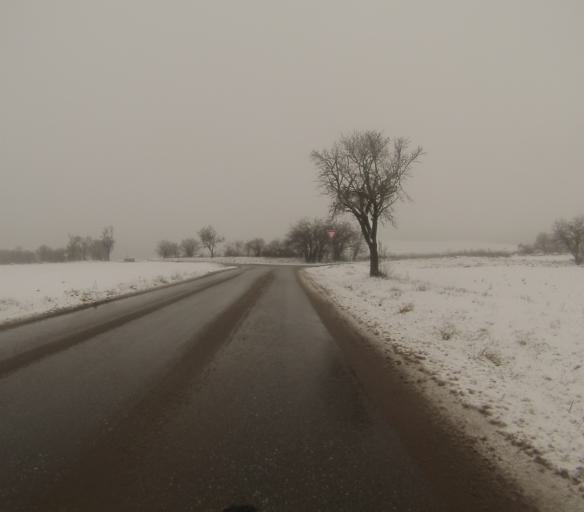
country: CZ
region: South Moravian
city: Ostopovice
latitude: 49.1619
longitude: 16.5298
